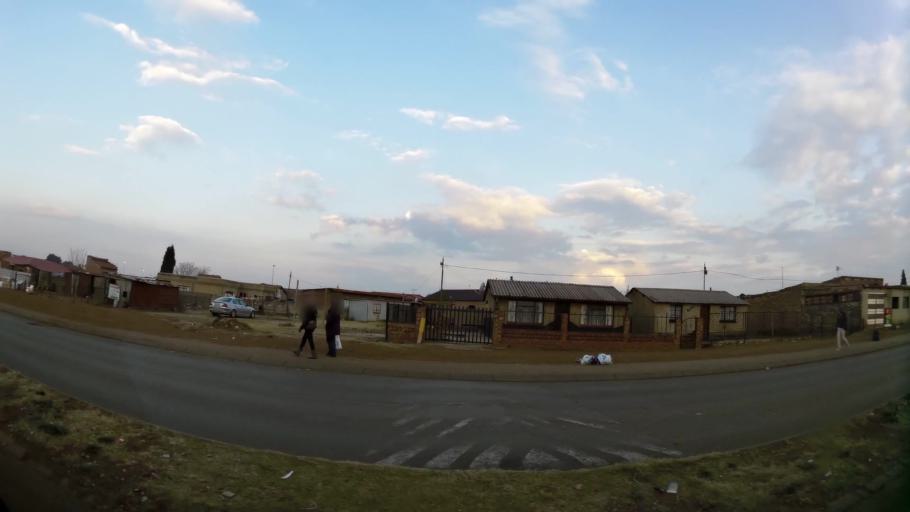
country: ZA
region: Gauteng
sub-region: City of Johannesburg Metropolitan Municipality
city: Orange Farm
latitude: -26.5673
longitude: 27.8485
